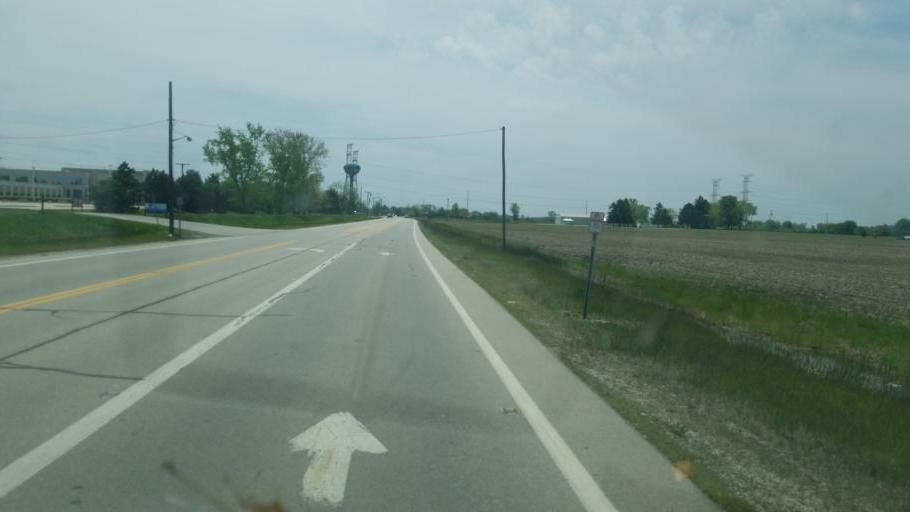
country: US
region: Ohio
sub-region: Ottawa County
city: Oak Harbor
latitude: 41.5989
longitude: -83.0968
